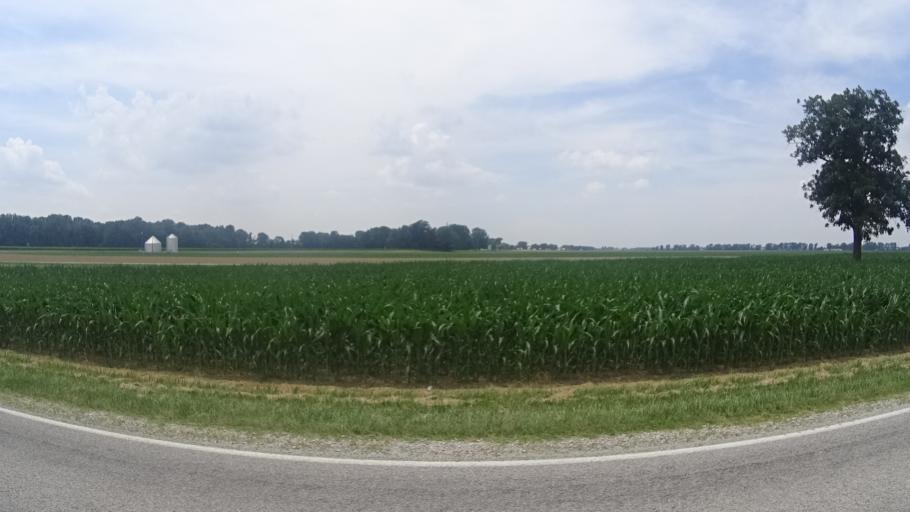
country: US
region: Ohio
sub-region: Erie County
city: Milan
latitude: 41.3087
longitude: -82.6336
